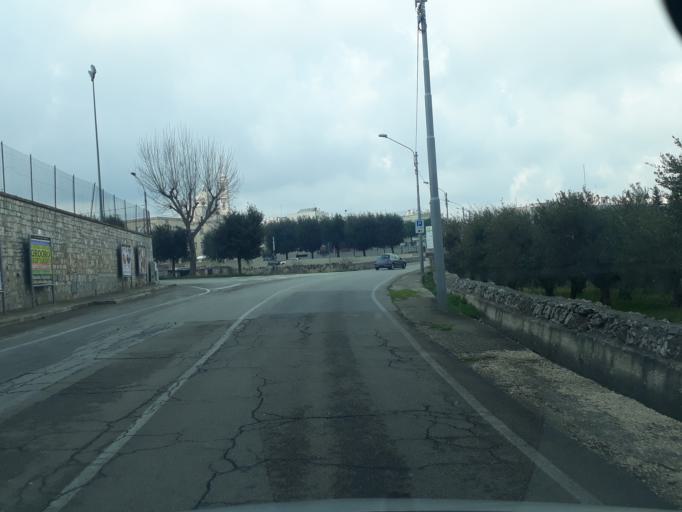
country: IT
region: Apulia
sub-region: Provincia di Bari
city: Locorotondo
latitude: 40.7535
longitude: 17.3356
